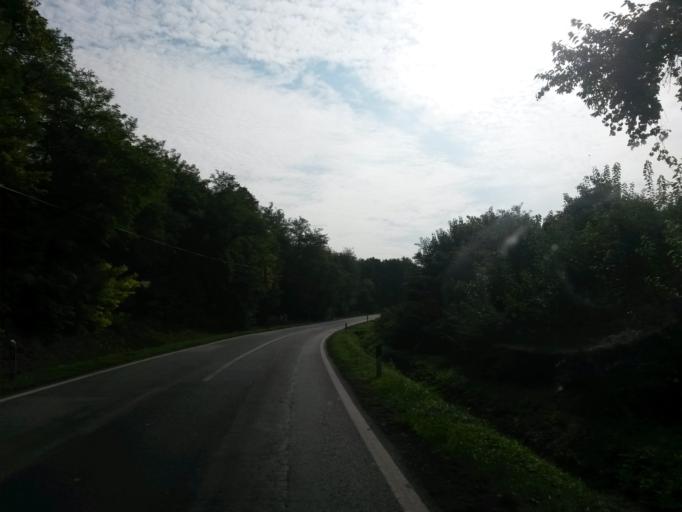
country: HR
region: Vukovarsko-Srijemska
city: Ilok
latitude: 45.2242
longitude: 19.3424
